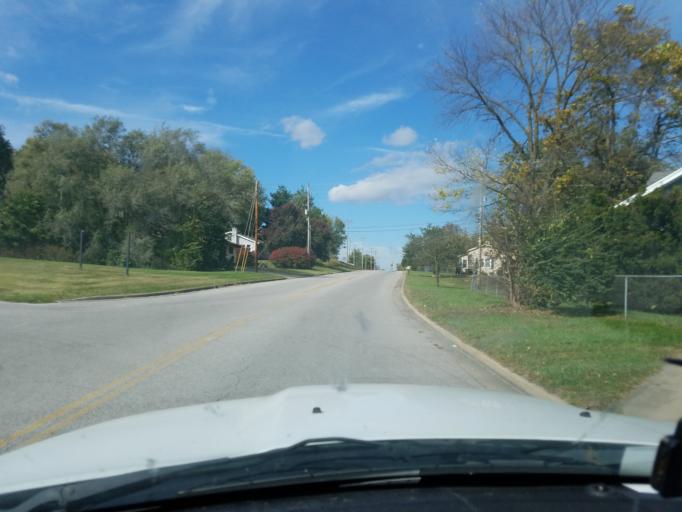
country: US
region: Indiana
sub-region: Clark County
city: Henryville
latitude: 38.4845
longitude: -85.7631
